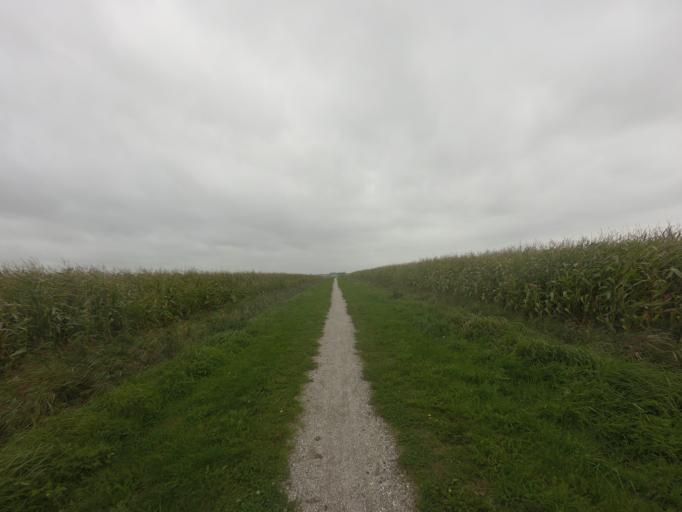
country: NL
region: Friesland
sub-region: Gemeente Ferwerderadiel
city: Ferwert
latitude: 53.3473
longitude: 5.8589
